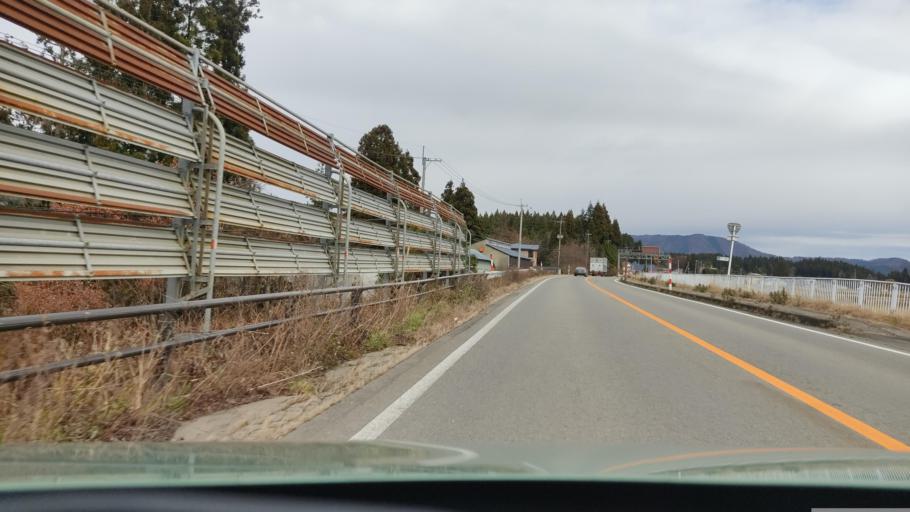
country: JP
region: Akita
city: Kakunodatemachi
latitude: 39.6099
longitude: 140.4218
